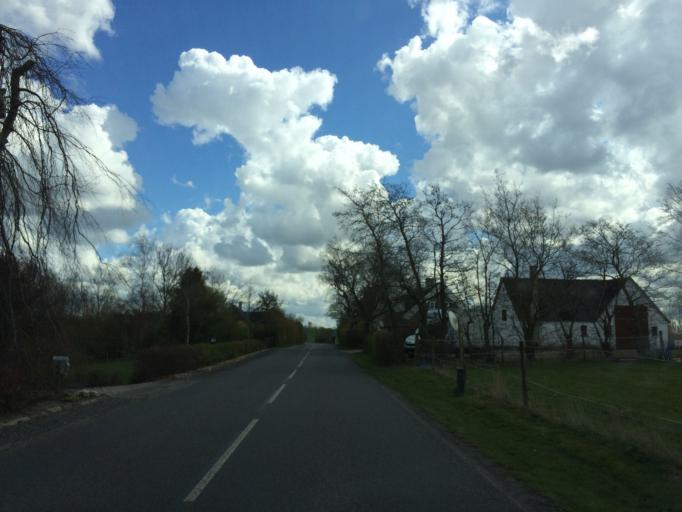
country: DK
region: South Denmark
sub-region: Assens Kommune
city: Tommerup
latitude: 55.2511
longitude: 10.2590
